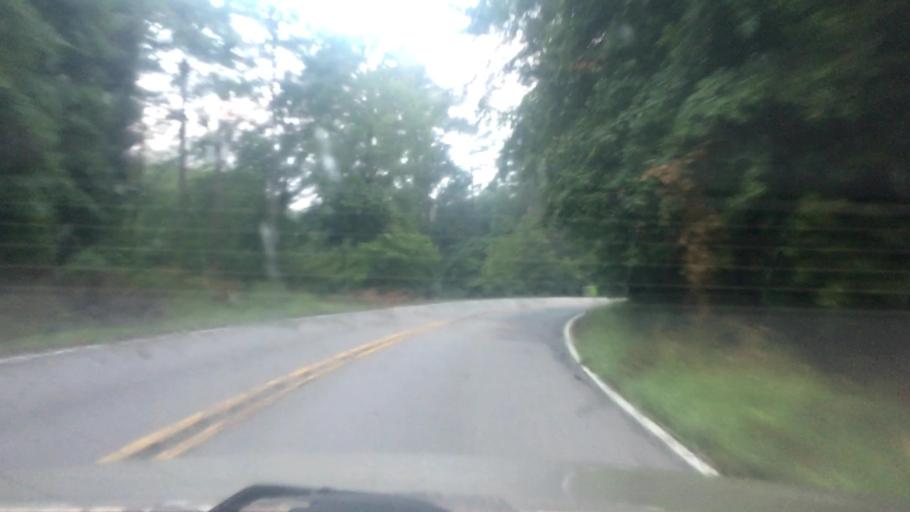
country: US
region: South Carolina
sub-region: Lexington County
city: Irmo
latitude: 34.1364
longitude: -81.1853
